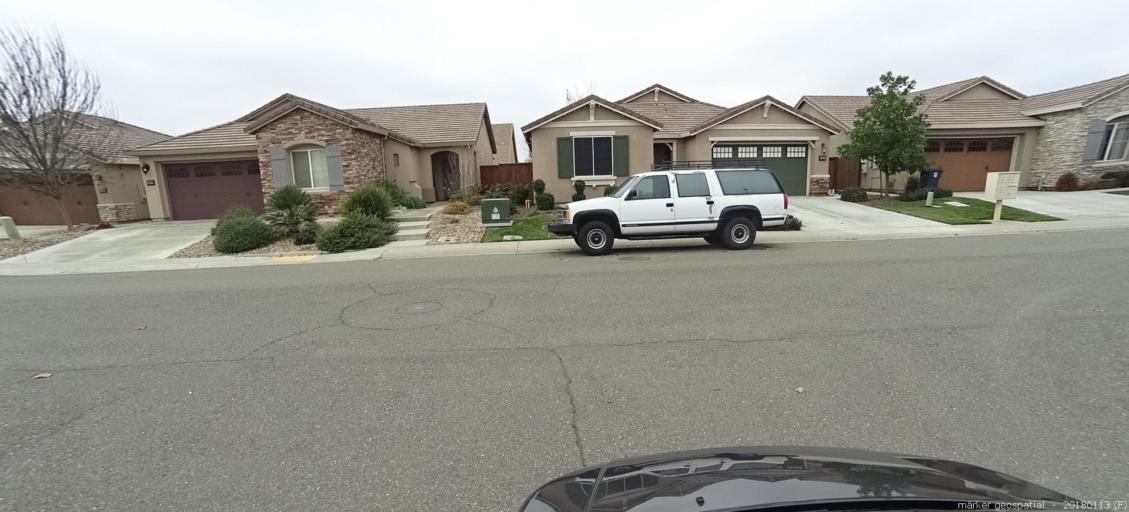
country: US
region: California
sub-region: Sacramento County
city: Gold River
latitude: 38.5580
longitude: -121.2134
